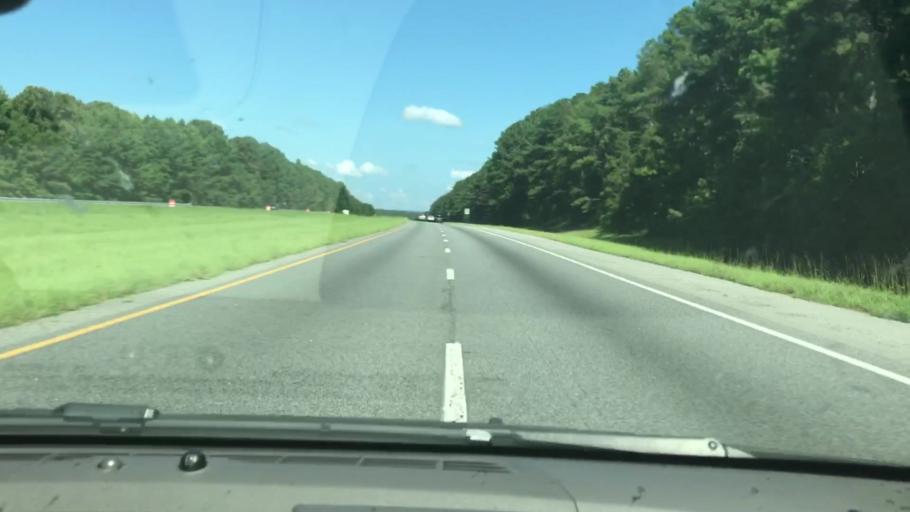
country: US
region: Georgia
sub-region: Harris County
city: Hamilton
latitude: 32.6250
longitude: -84.9557
